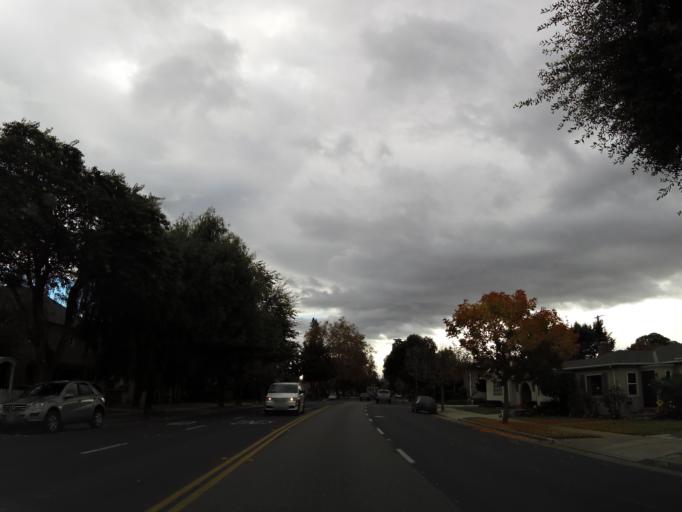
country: US
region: California
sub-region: Santa Clara County
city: Buena Vista
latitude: 37.3004
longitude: -121.8941
